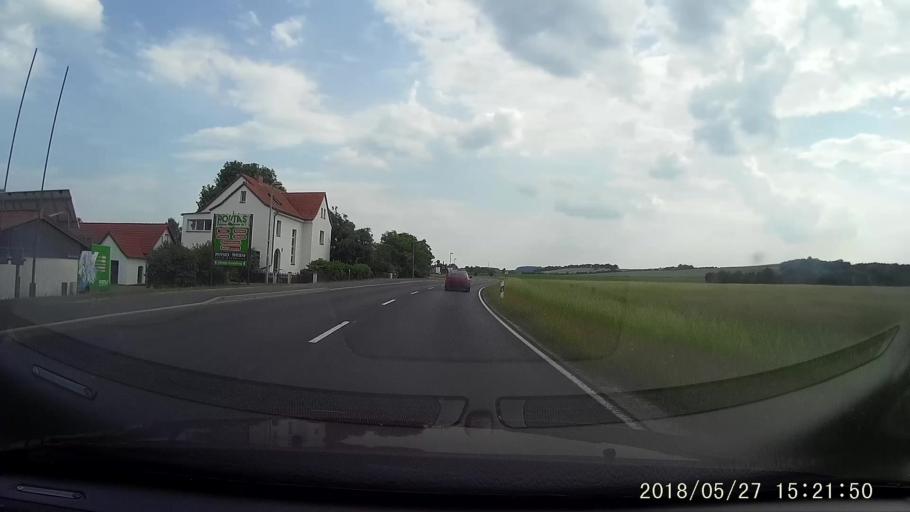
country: DE
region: Saxony
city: Kodersdorf
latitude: 51.2380
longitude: 14.8895
